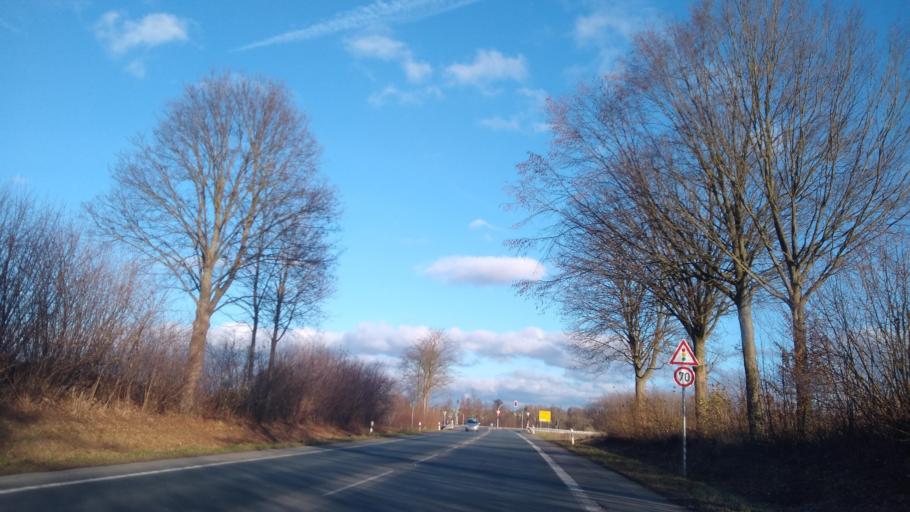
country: DE
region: North Rhine-Westphalia
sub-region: Regierungsbezirk Detmold
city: Steinheim
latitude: 51.8809
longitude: 9.0911
